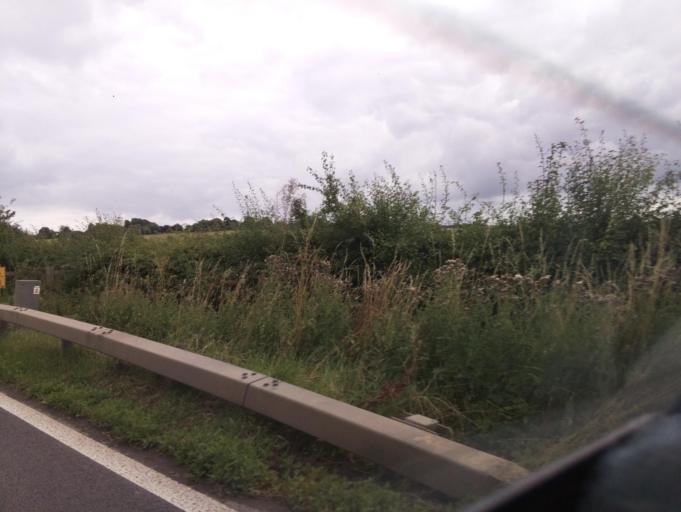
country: GB
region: England
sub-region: Lincolnshire
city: Barrowby
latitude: 52.9258
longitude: -0.6994
